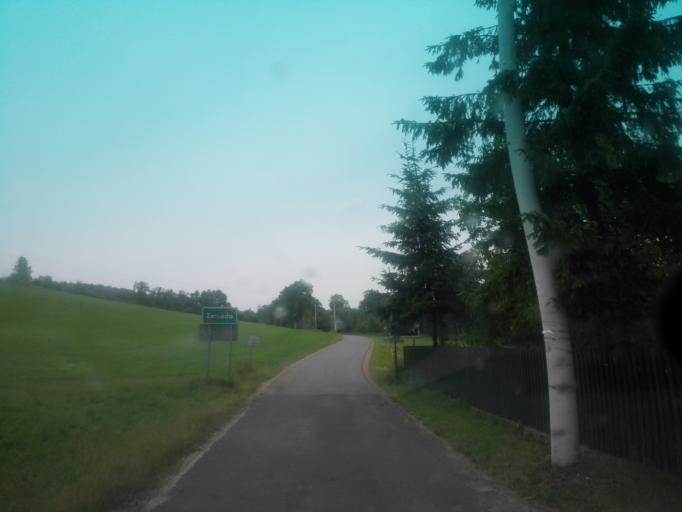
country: PL
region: Silesian Voivodeship
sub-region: Powiat czestochowski
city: Mstow
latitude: 50.8265
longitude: 19.3107
